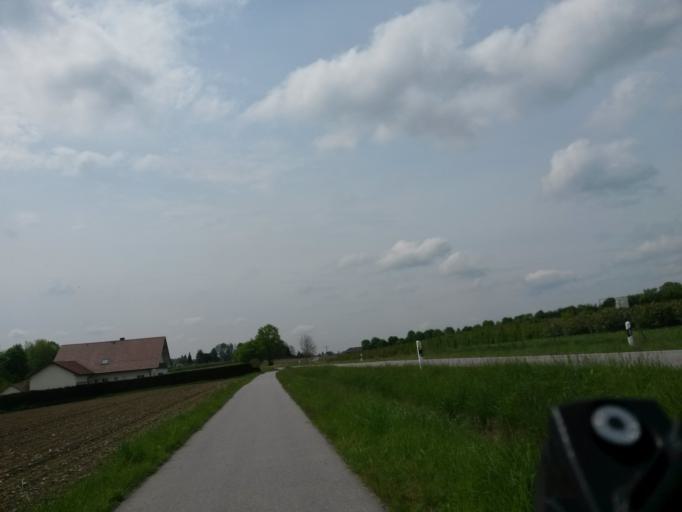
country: DE
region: Baden-Wuerttemberg
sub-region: Tuebingen Region
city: Bad Waldsee
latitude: 47.9344
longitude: 9.7473
